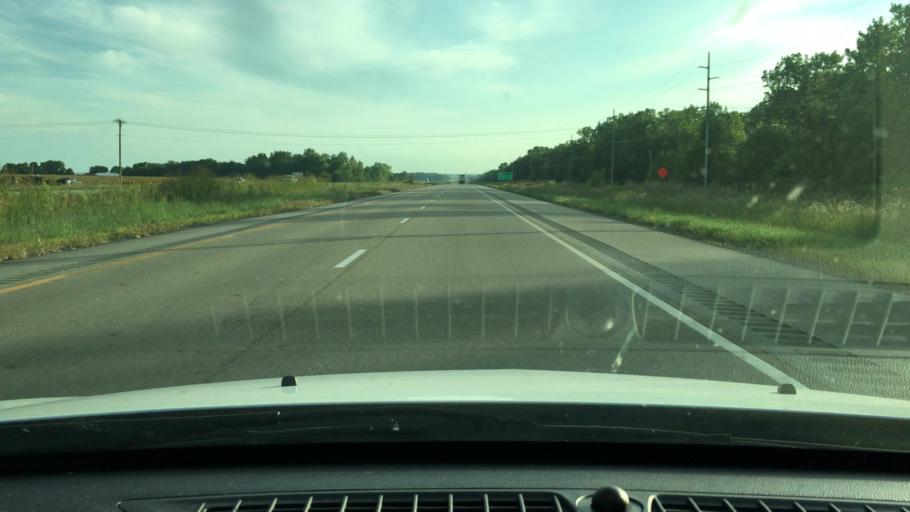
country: US
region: Illinois
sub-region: Logan County
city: Atlanta
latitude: 40.2460
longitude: -89.2487
